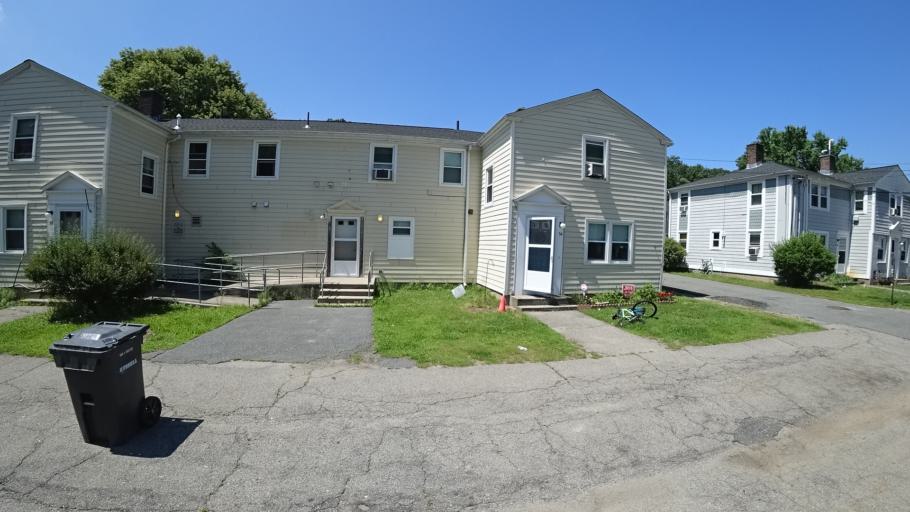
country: US
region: Massachusetts
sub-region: Norfolk County
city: Dedham
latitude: 42.2457
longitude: -71.1461
